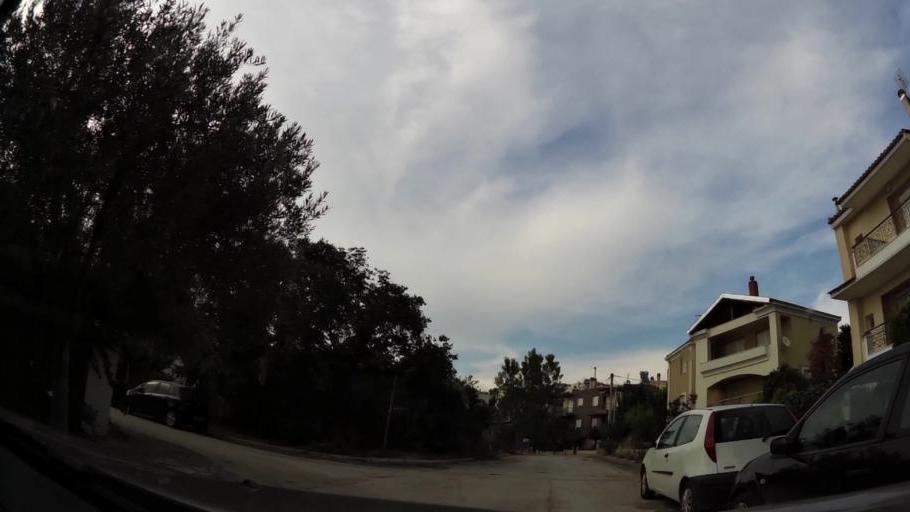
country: GR
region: Central Macedonia
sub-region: Nomos Thessalonikis
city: Pefka
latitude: 40.6604
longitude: 22.9836
